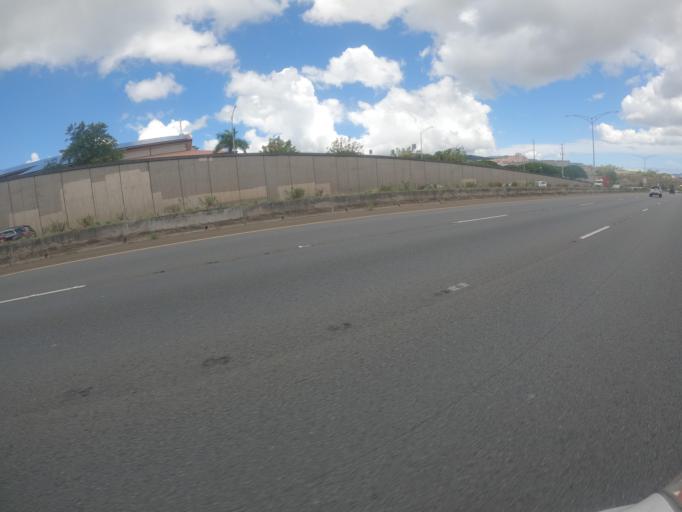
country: US
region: Hawaii
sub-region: Honolulu County
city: Halawa Heights
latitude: 21.3649
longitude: -157.9030
